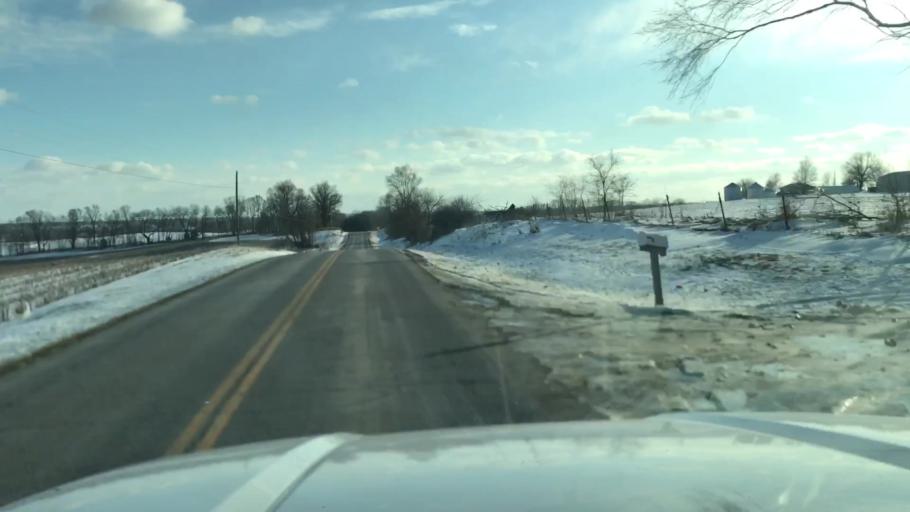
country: US
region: Missouri
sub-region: Andrew County
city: Savannah
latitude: 40.0499
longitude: -94.9750
